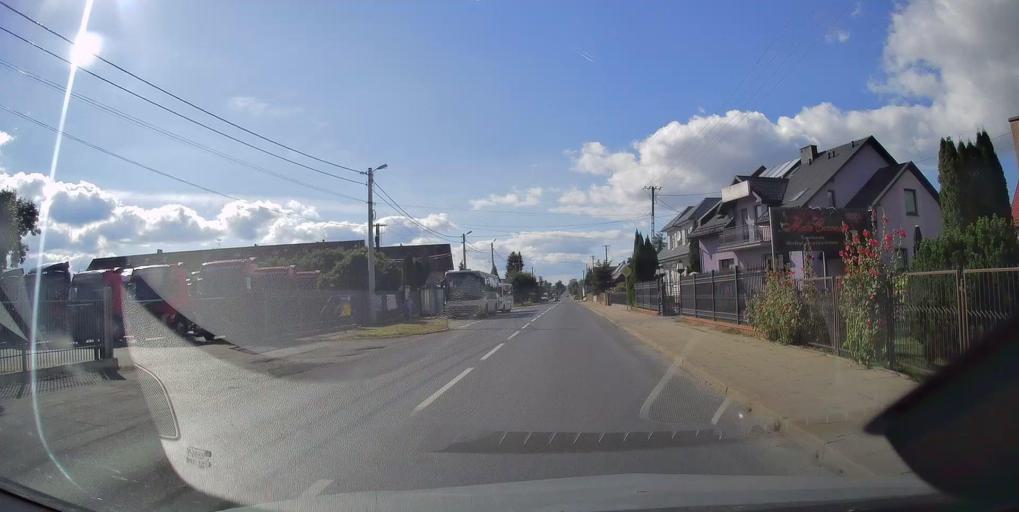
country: PL
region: Swietokrzyskie
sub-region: Powiat kielecki
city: Bodzentyn
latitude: 50.9427
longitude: 20.9454
